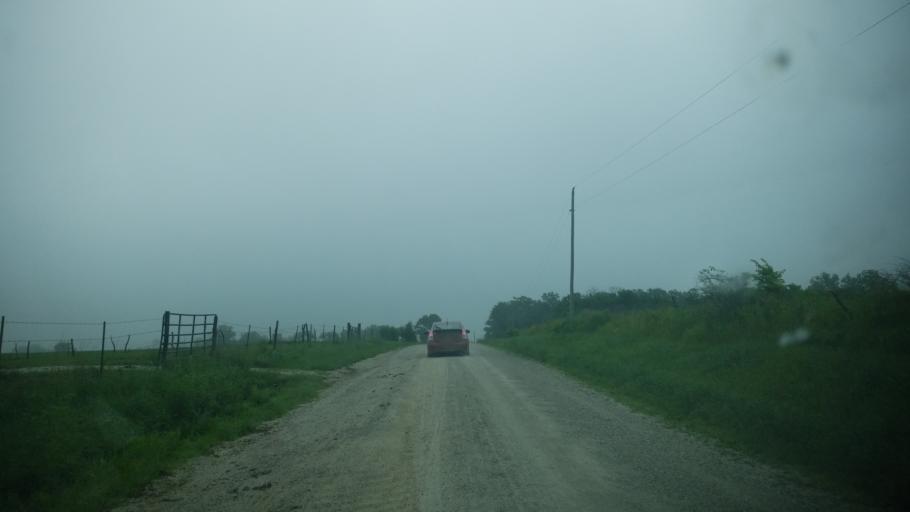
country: US
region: Missouri
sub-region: Pike County
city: Bowling Green
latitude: 39.3087
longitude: -91.3228
